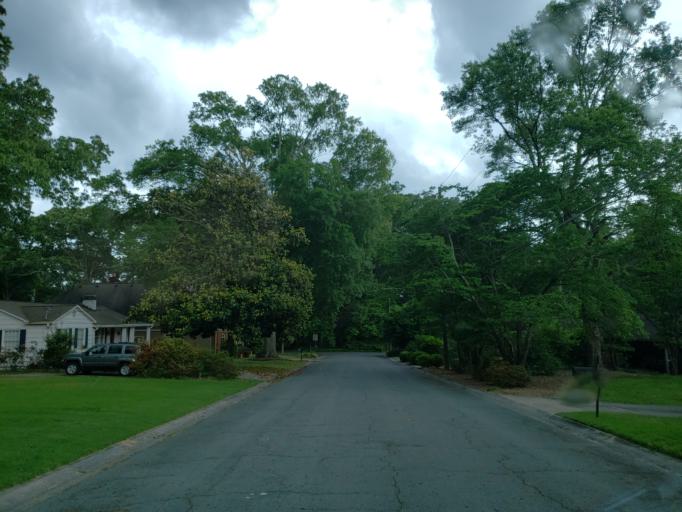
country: US
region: Georgia
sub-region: Cobb County
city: Marietta
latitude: 33.9551
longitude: -84.5685
